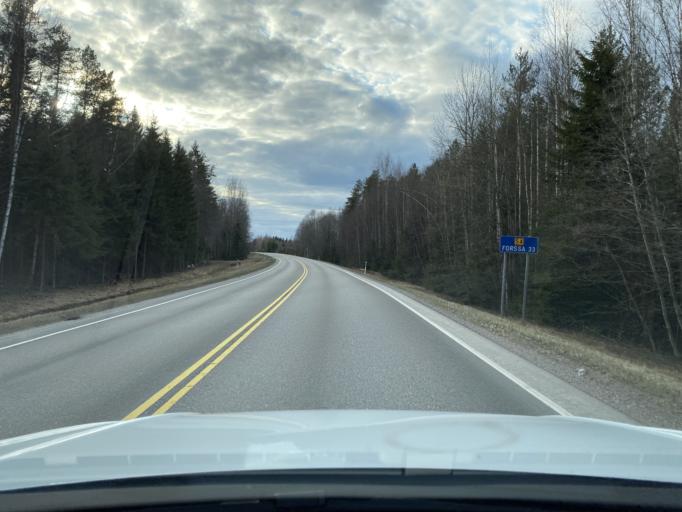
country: FI
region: Haeme
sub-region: Haemeenlinna
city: Renko
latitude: 60.7820
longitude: 24.1603
